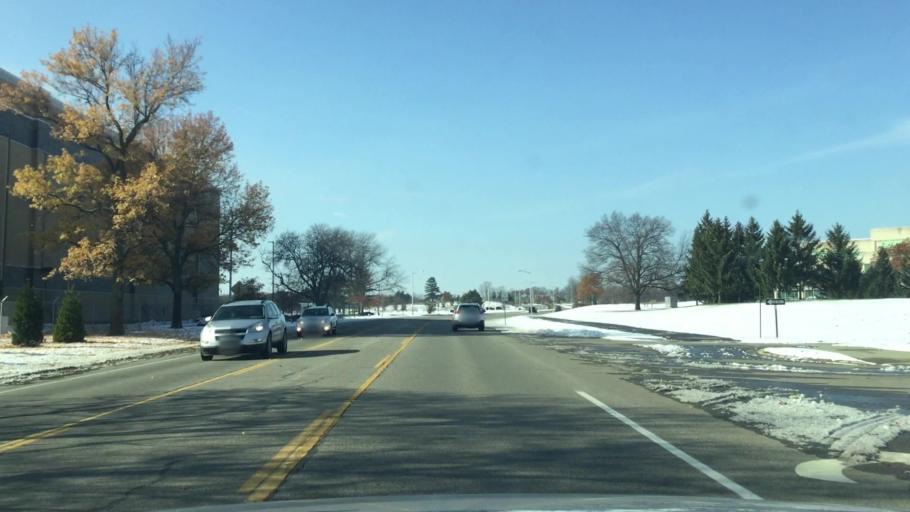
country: US
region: Michigan
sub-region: Kalamazoo County
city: Portage
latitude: 42.2156
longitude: -85.5546
